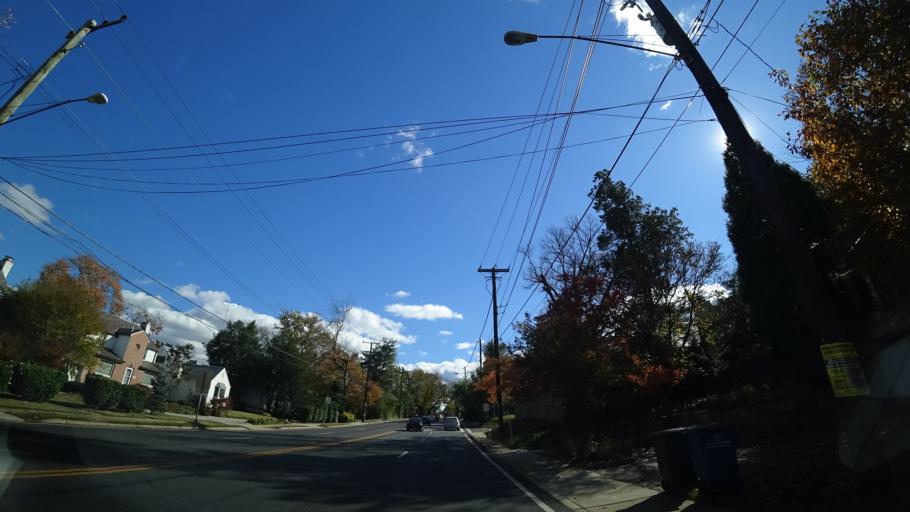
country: US
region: Maryland
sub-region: Montgomery County
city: Friendship Village
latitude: 38.9573
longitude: -77.0924
